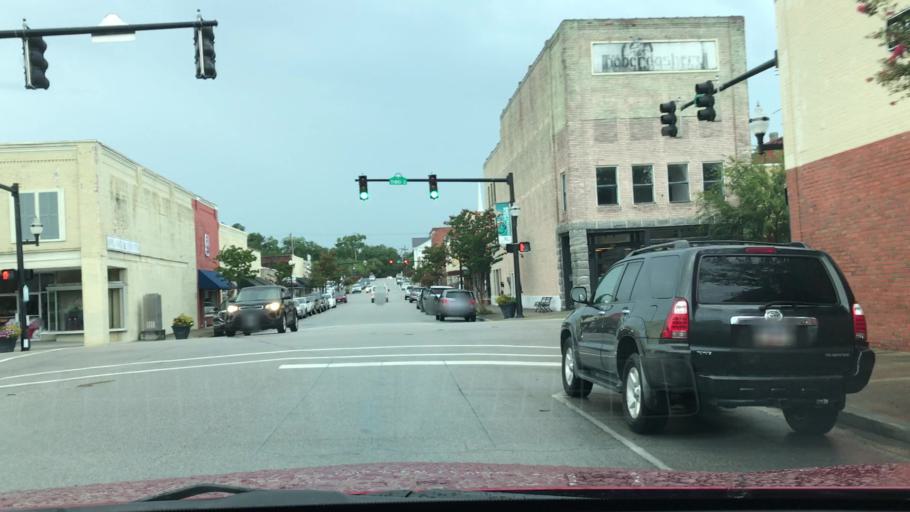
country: US
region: South Carolina
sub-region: Horry County
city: Conway
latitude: 33.8346
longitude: -79.0470
